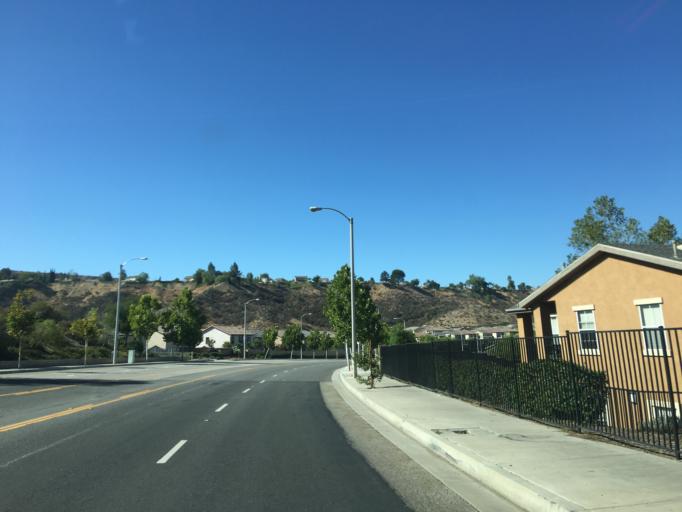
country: US
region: California
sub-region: Los Angeles County
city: Santa Clarita
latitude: 34.4456
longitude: -118.4837
